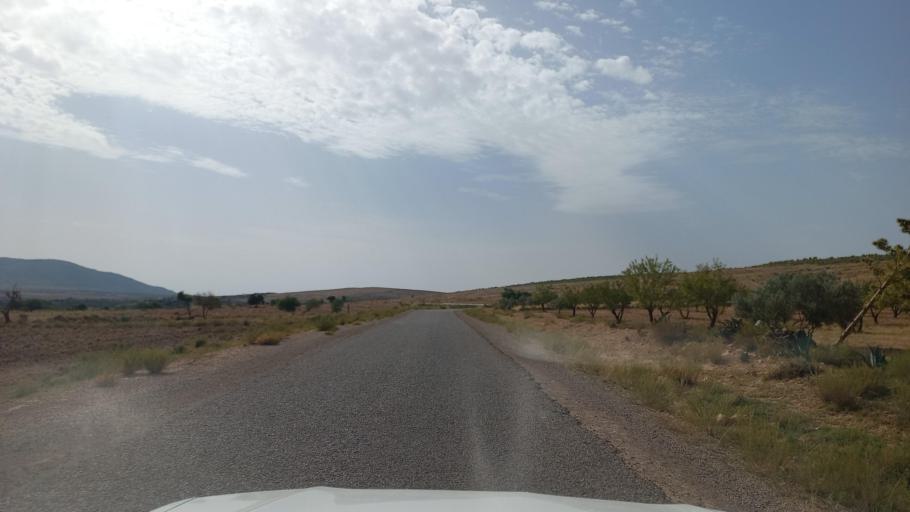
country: TN
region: Al Qasrayn
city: Kasserine
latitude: 35.3683
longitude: 8.8655
